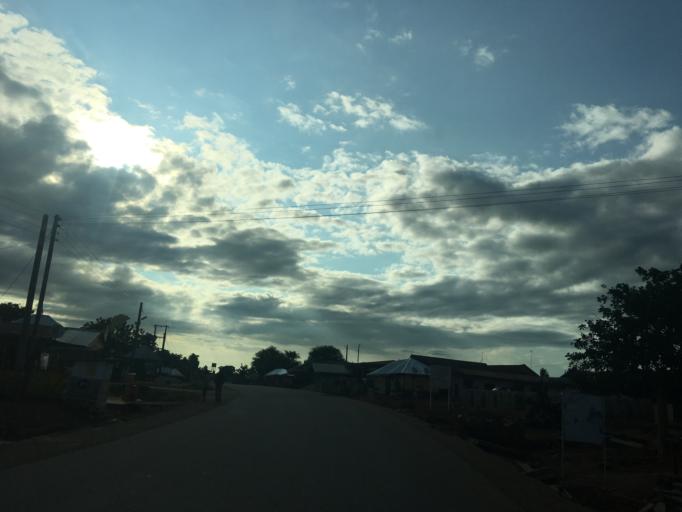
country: GH
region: Western
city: Bibiani
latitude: 6.3291
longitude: -2.2504
